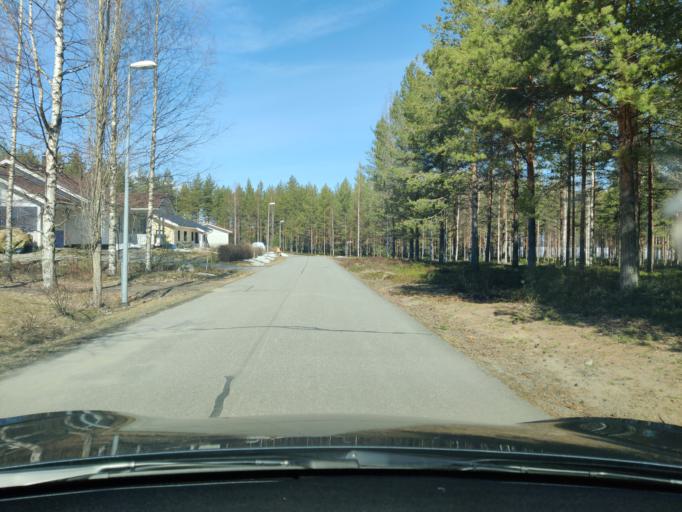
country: FI
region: Northern Savo
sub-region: Kuopio
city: Vehmersalmi
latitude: 62.7726
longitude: 27.9856
